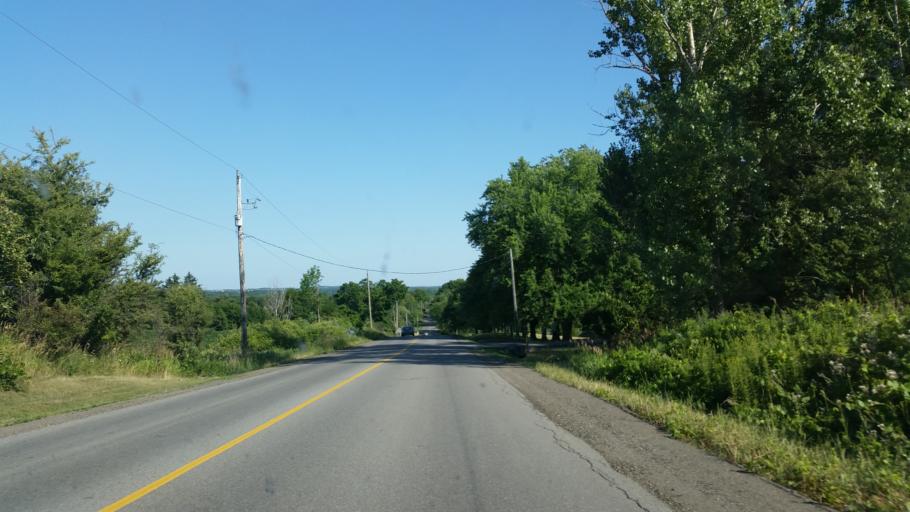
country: CA
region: Ontario
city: Bradford West Gwillimbury
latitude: 43.9563
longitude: -79.7721
